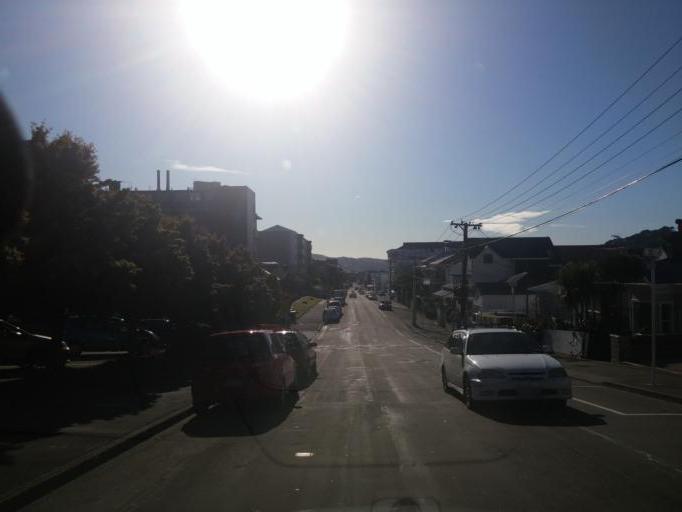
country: NZ
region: Wellington
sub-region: Wellington City
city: Wellington
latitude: -41.3095
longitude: 174.7760
